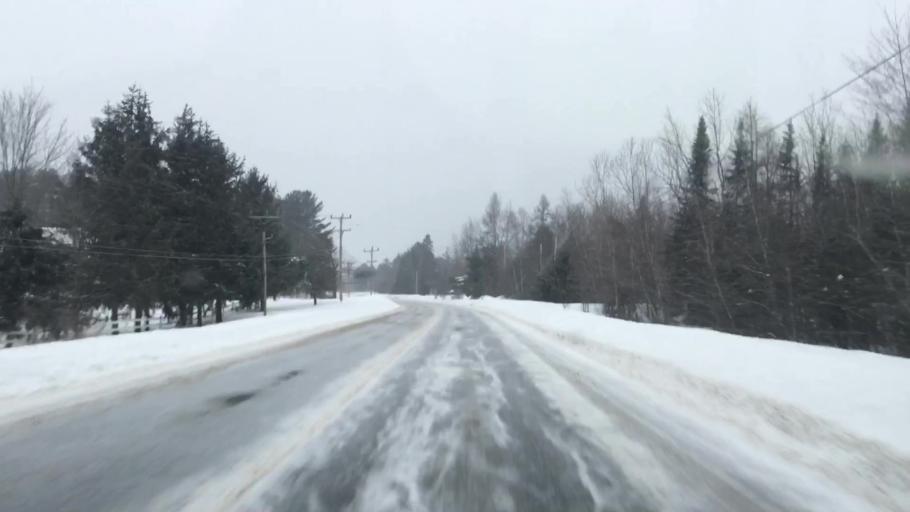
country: US
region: Maine
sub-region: Penobscot County
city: Medway
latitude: 45.5423
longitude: -68.3697
